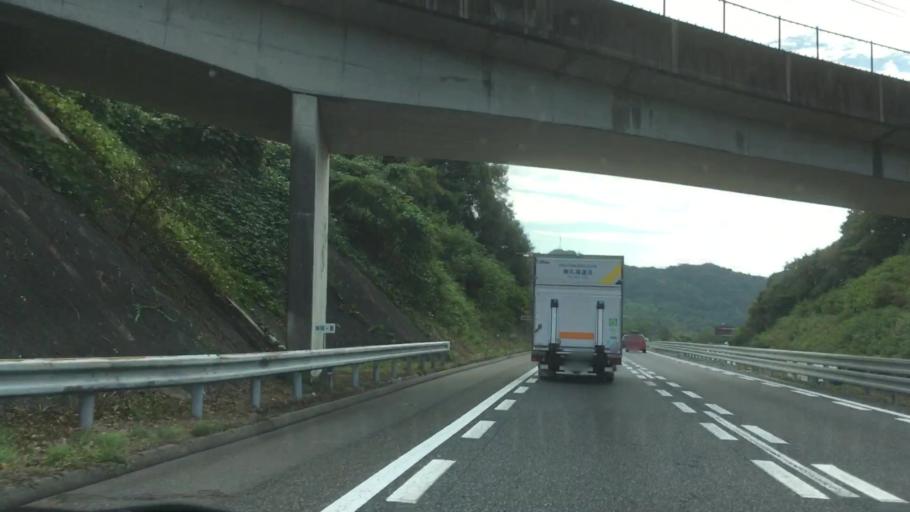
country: JP
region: Yamaguchi
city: Iwakuni
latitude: 34.1079
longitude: 132.1139
